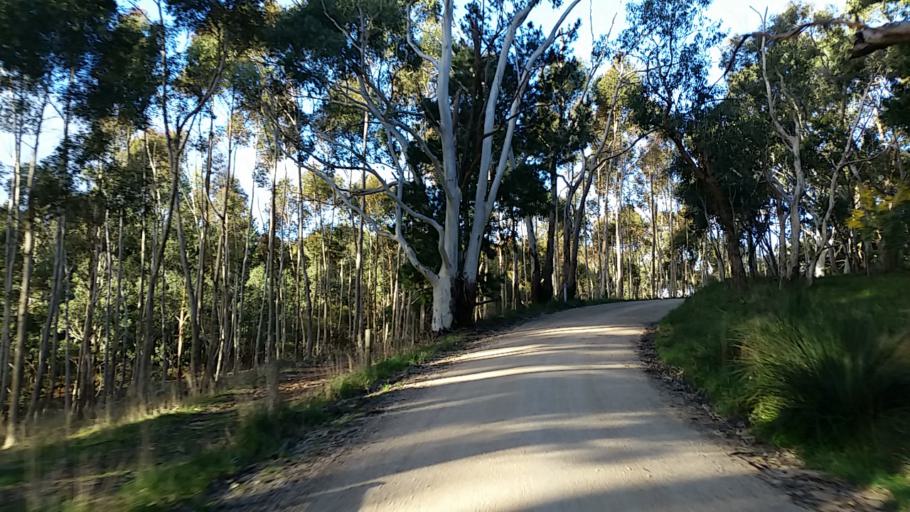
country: AU
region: South Australia
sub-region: Adelaide Hills
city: Lobethal
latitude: -34.9030
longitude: 138.8061
